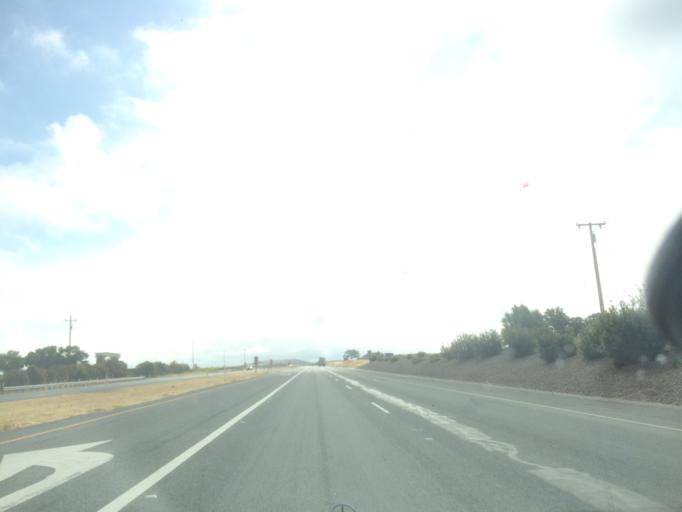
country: US
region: California
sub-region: San Luis Obispo County
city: Paso Robles
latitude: 35.6593
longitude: -120.5716
